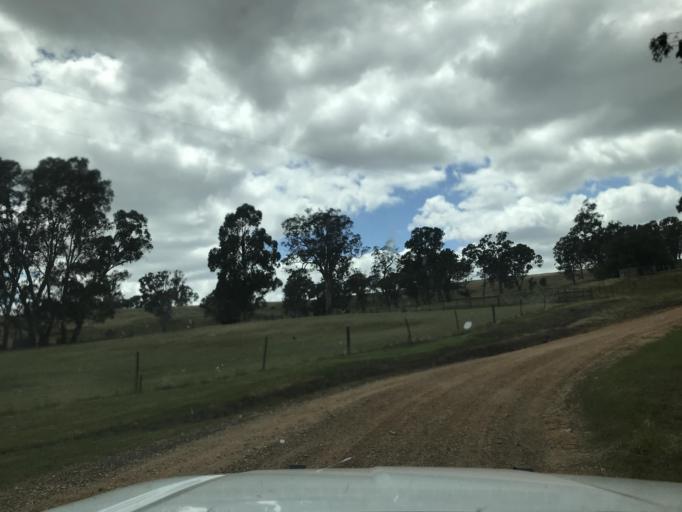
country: AU
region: South Australia
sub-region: Wattle Range
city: Penola
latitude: -37.3657
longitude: 141.2447
